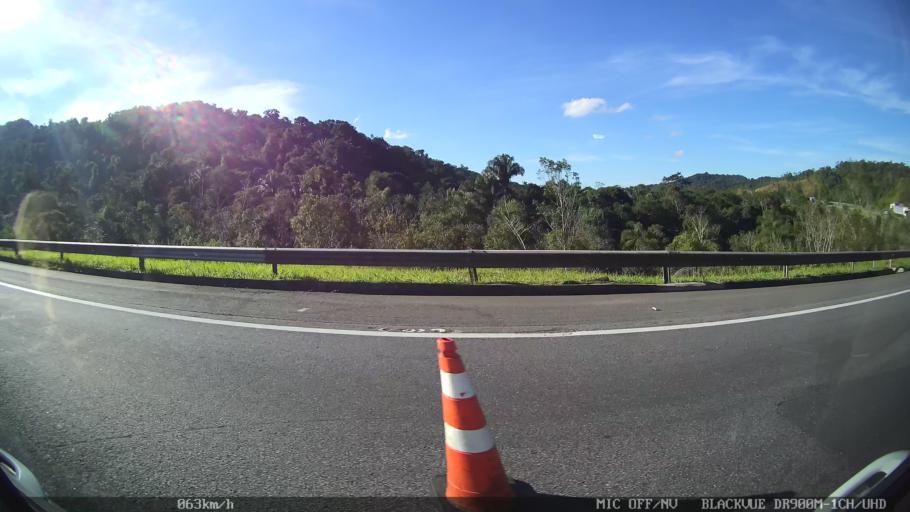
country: BR
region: Parana
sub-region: Antonina
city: Antonina
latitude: -25.0973
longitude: -48.6595
